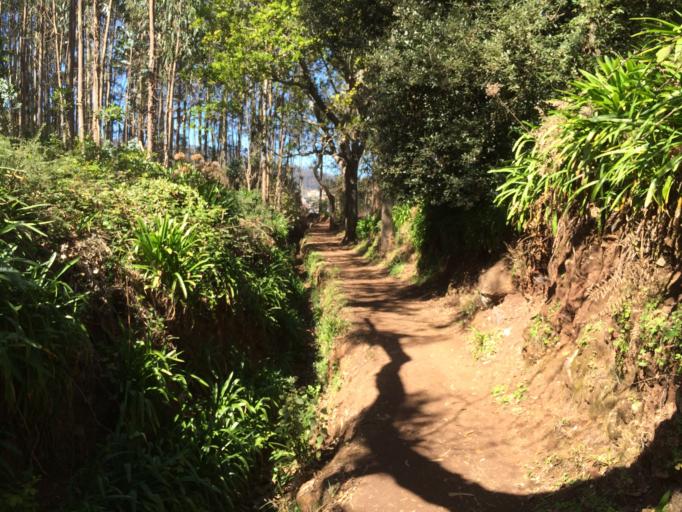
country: PT
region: Madeira
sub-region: Santa Cruz
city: Camacha
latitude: 32.6780
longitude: -16.8540
